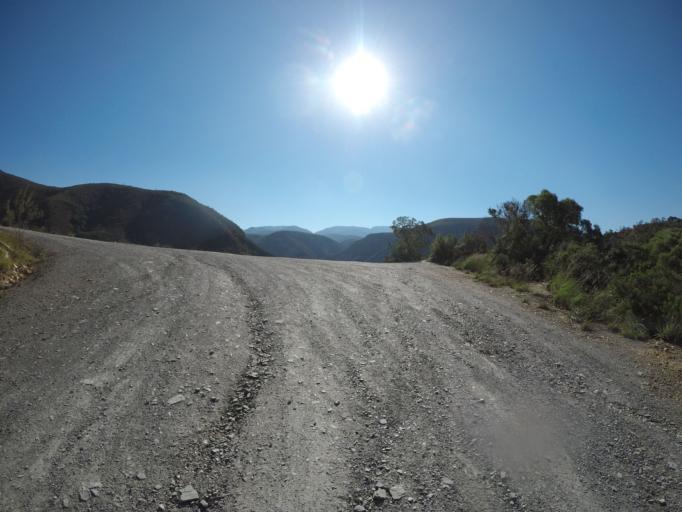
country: ZA
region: Eastern Cape
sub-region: Cacadu District Municipality
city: Kareedouw
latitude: -33.6539
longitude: 24.5086
